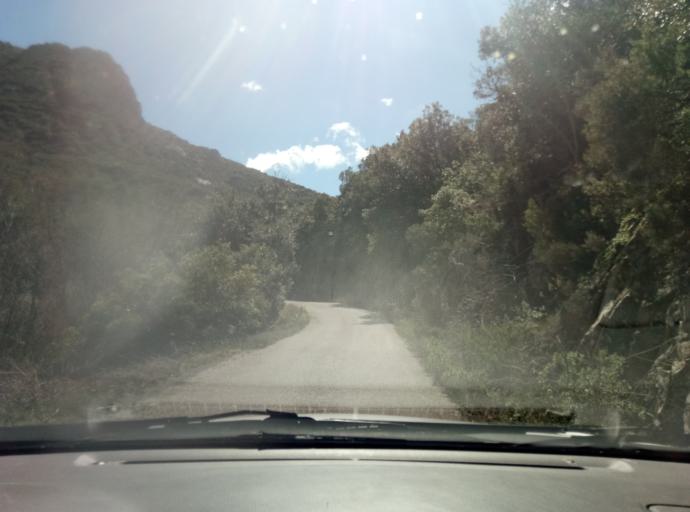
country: ES
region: Catalonia
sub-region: Provincia de Tarragona
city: Vimbodi
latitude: 41.3573
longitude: 1.0606
